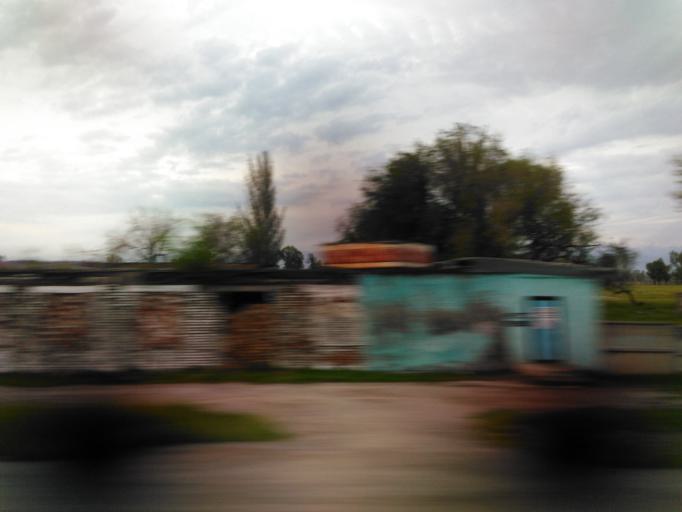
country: KG
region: Chuy
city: Bishkek
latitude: 42.9368
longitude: 74.5089
